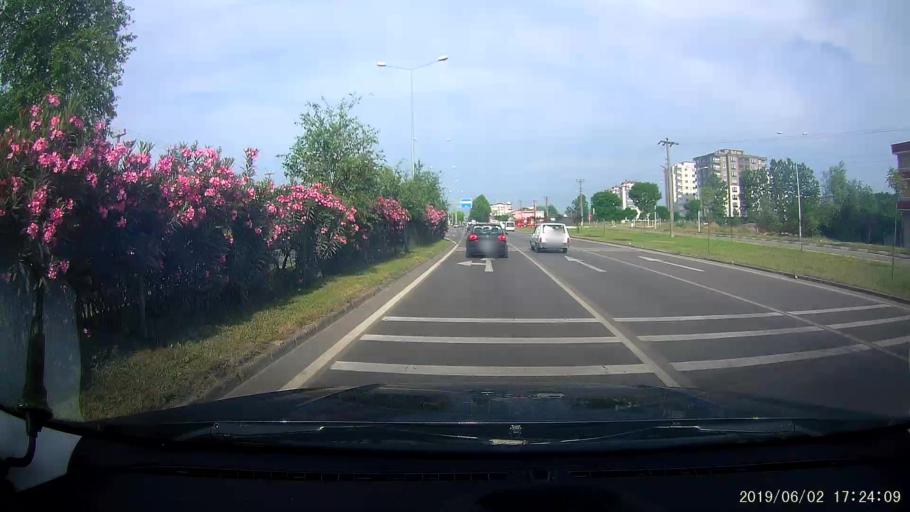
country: TR
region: Samsun
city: Carsamba
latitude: 41.2059
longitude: 36.6975
